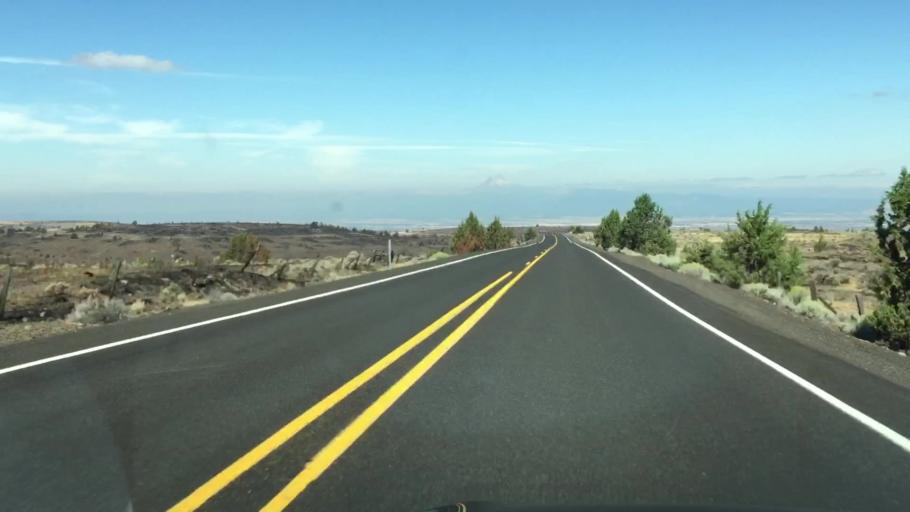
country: US
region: Oregon
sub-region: Jefferson County
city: Warm Springs
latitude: 45.0552
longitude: -121.0202
